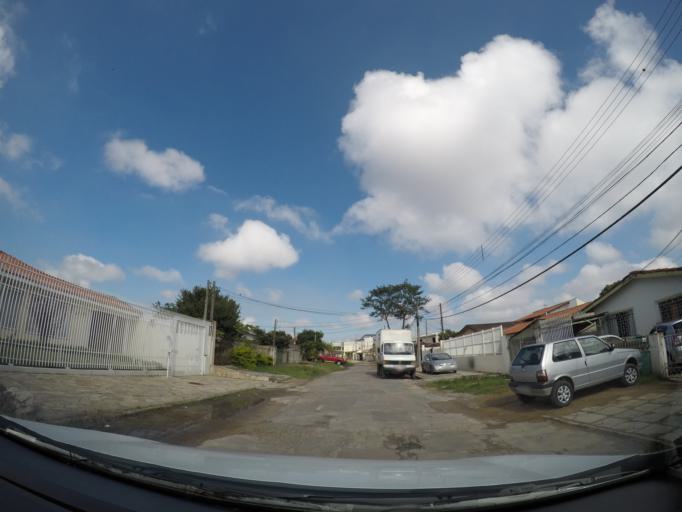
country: BR
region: Parana
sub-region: Sao Jose Dos Pinhais
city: Sao Jose dos Pinhais
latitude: -25.4967
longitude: -49.2198
